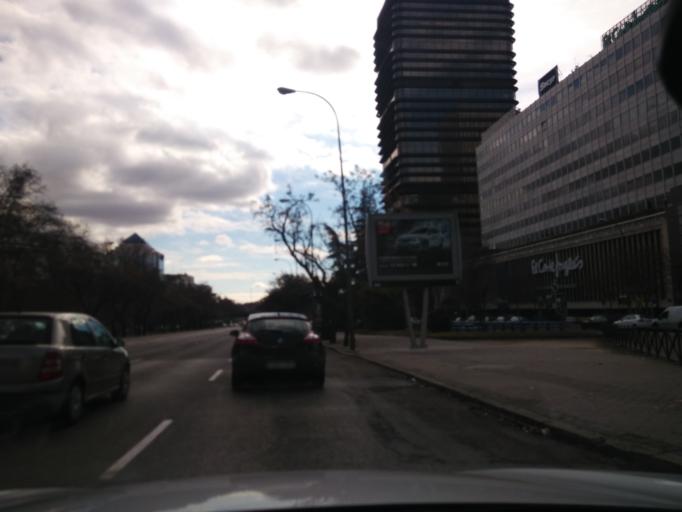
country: ES
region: Madrid
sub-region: Provincia de Madrid
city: Chamartin
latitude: 40.4492
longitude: -3.6911
